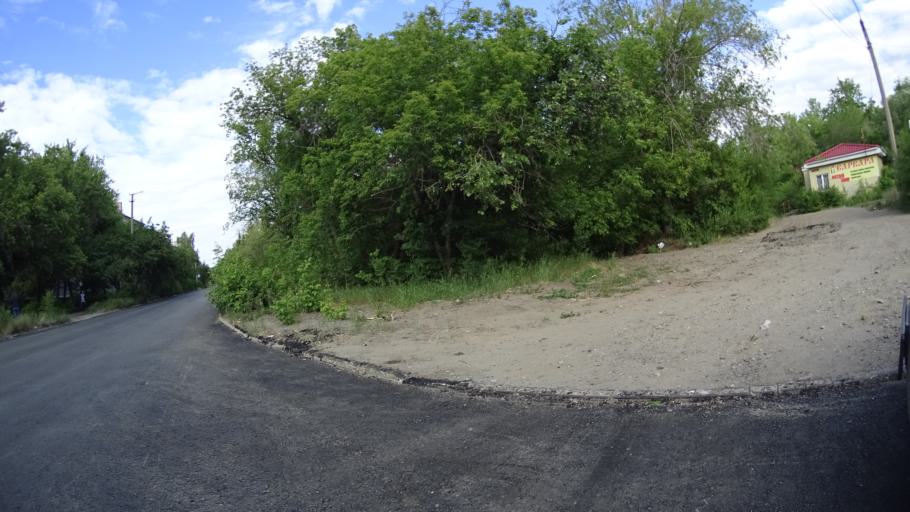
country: RU
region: Chelyabinsk
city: Troitsk
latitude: 54.0471
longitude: 61.6312
